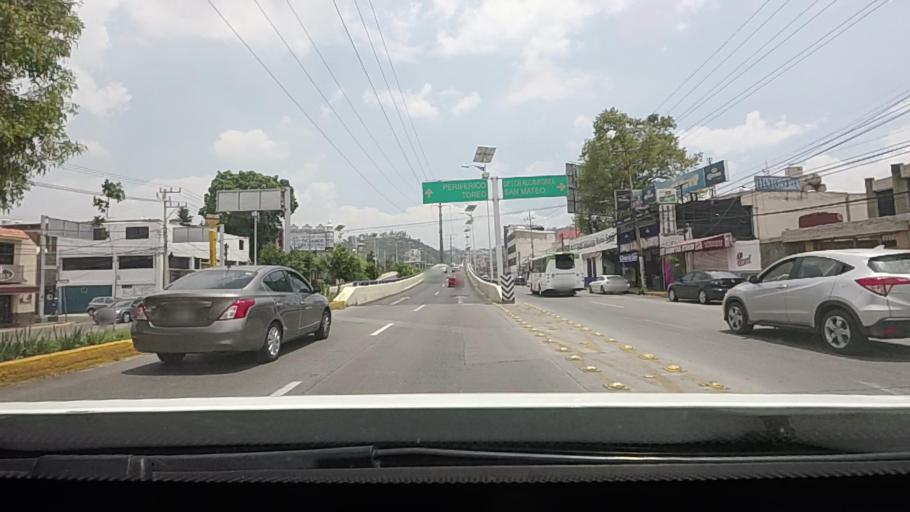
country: MX
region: Mexico
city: Naucalpan de Juarez
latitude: 19.4935
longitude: -99.2533
